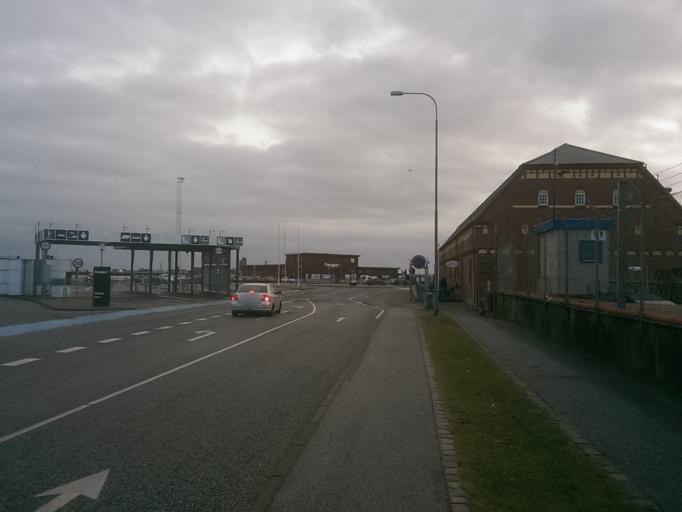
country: DK
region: South Denmark
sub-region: Esbjerg Kommune
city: Esbjerg
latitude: 55.4625
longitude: 8.4409
